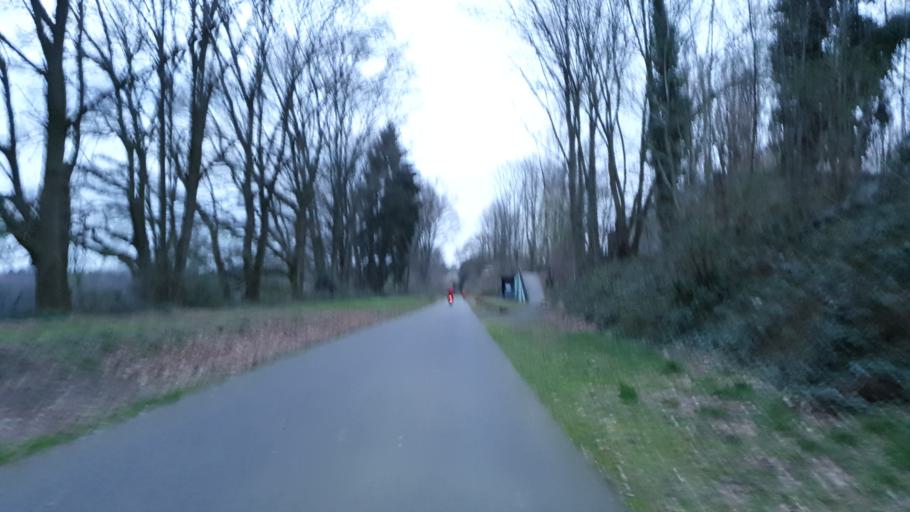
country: DE
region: North Rhine-Westphalia
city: Leichlingen
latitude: 51.0912
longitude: 7.0618
